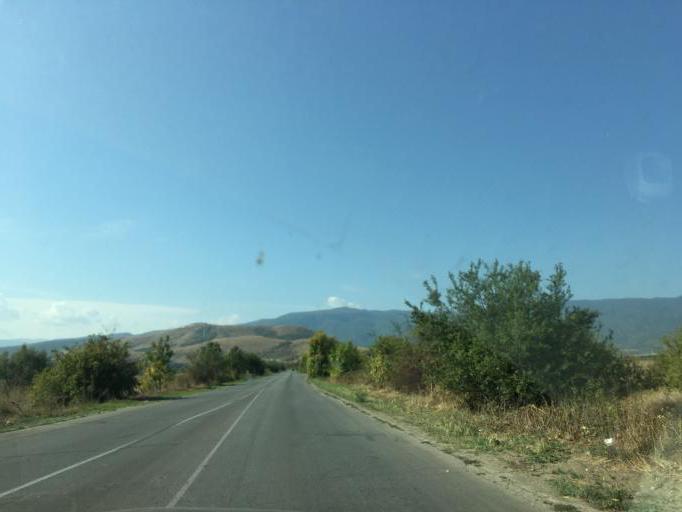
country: BG
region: Pazardzhik
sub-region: Obshtina Pazardzhik
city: Pazardzhik
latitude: 42.1379
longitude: 24.2981
